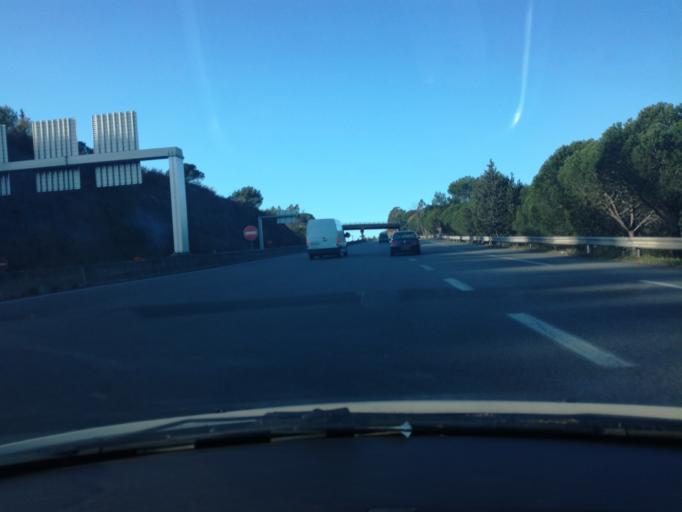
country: FR
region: Provence-Alpes-Cote d'Azur
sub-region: Departement du Var
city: Frejus
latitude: 43.4682
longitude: 6.7261
